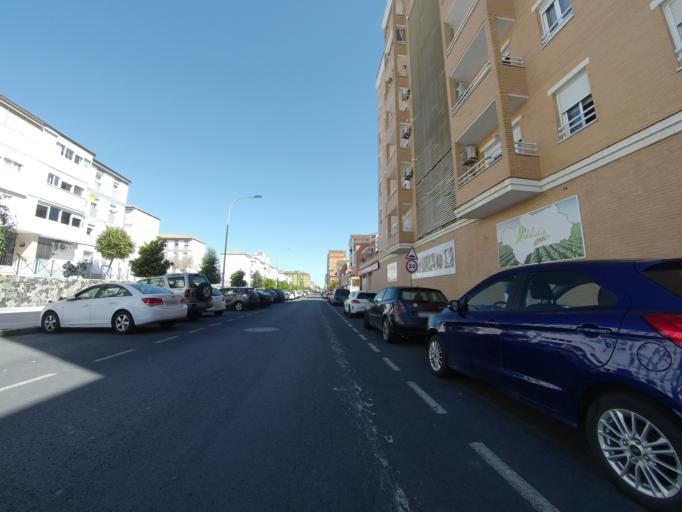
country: ES
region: Andalusia
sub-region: Provincia de Huelva
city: Huelva
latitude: 37.2684
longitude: -6.9365
